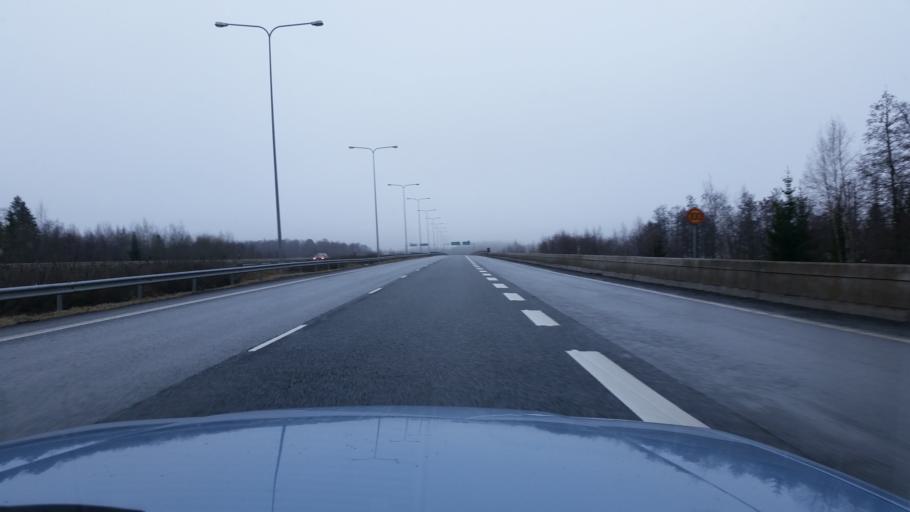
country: FI
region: Pirkanmaa
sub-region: Etelae-Pirkanmaa
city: Toijala
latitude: 61.2171
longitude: 23.8390
